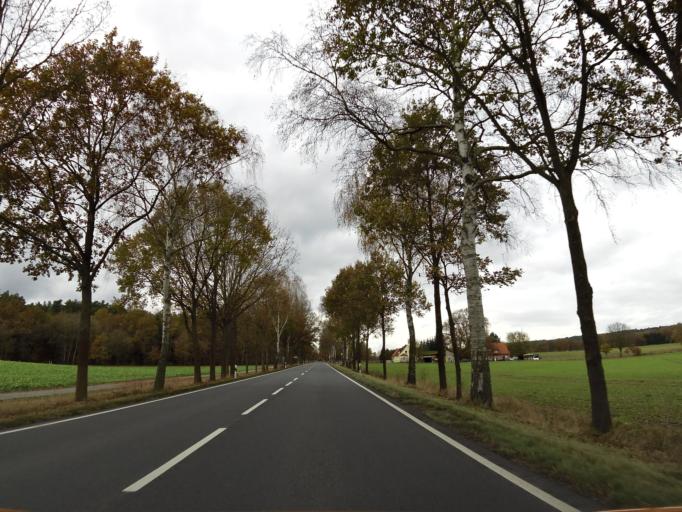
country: DE
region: Lower Saxony
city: Schnega
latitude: 52.9102
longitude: 10.8995
